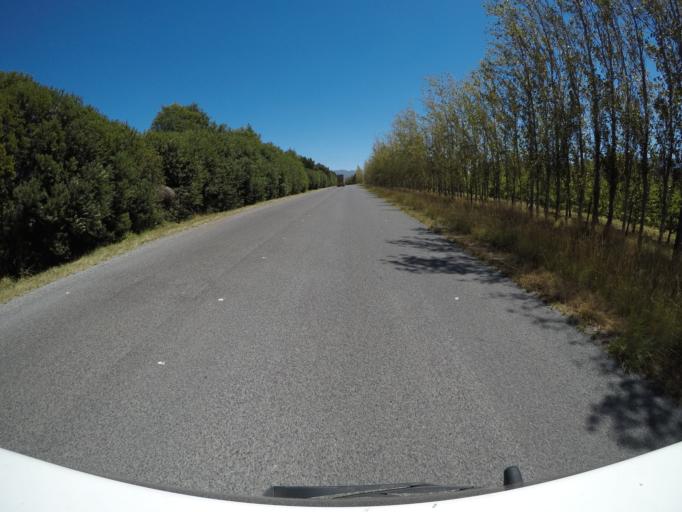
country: ZA
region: Western Cape
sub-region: Overberg District Municipality
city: Grabouw
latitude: -34.1852
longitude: 19.0386
